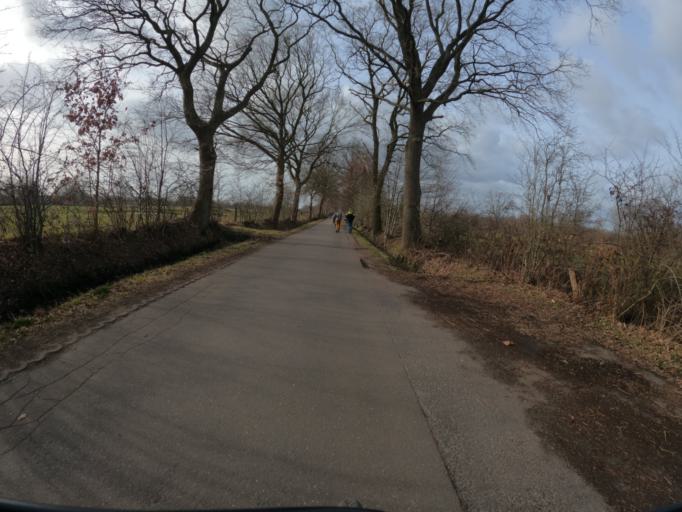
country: DE
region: Schleswig-Holstein
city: Halstenbek
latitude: 53.5866
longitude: 9.8083
